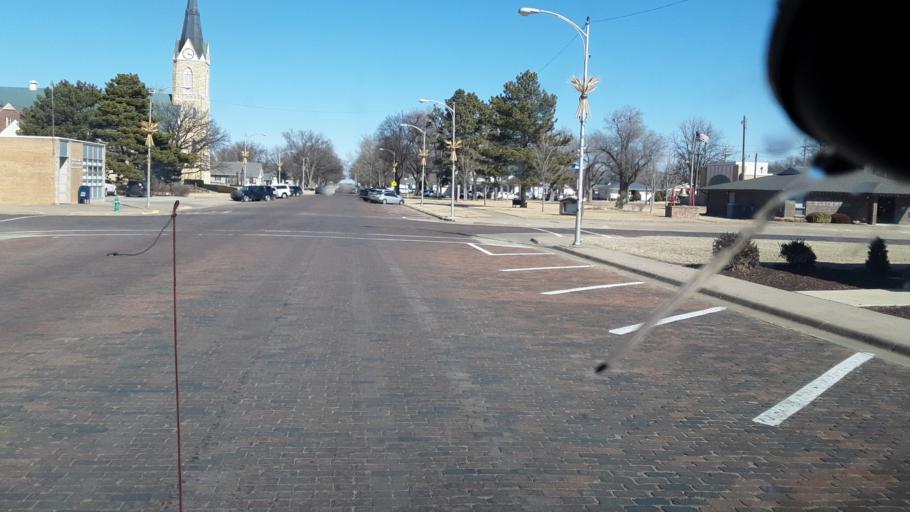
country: US
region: Kansas
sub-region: Barton County
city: Ellinwood
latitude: 38.3553
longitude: -98.5812
